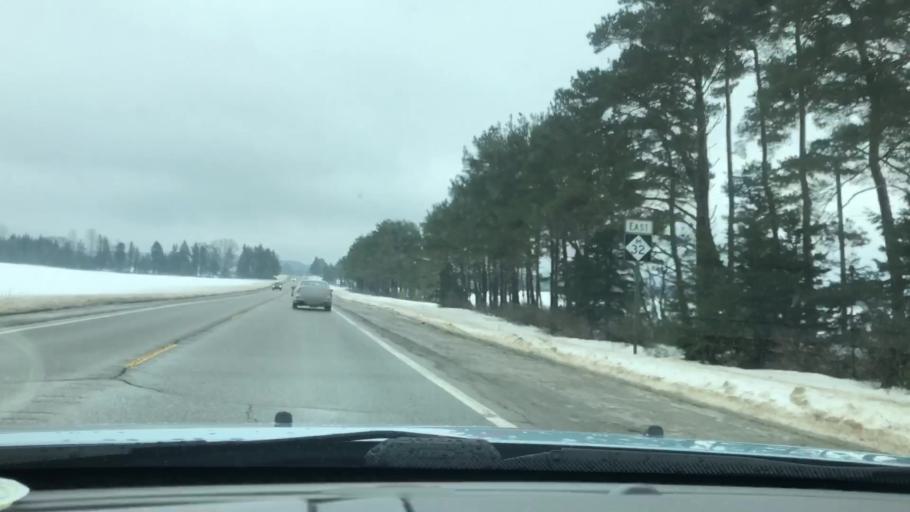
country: US
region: Michigan
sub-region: Charlevoix County
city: Boyne City
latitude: 45.0664
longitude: -84.8772
